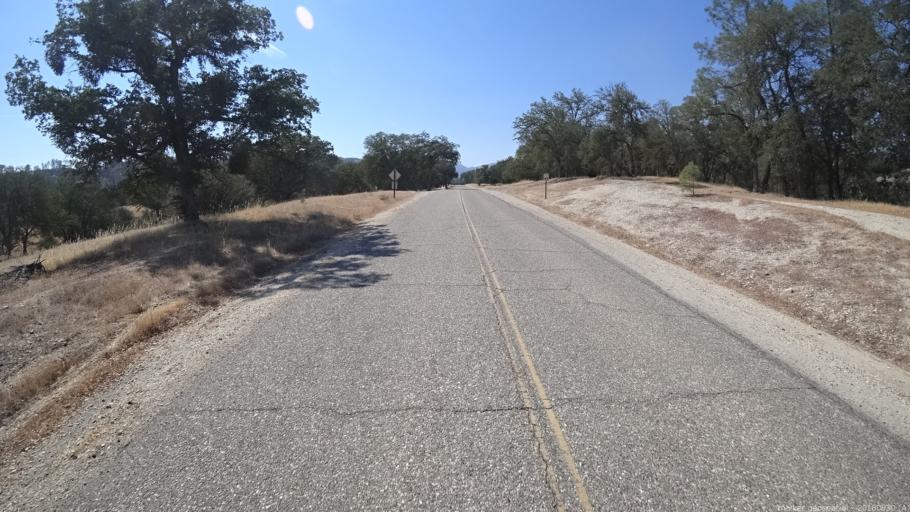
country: US
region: California
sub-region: Monterey County
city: King City
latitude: 36.0003
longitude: -121.2553
